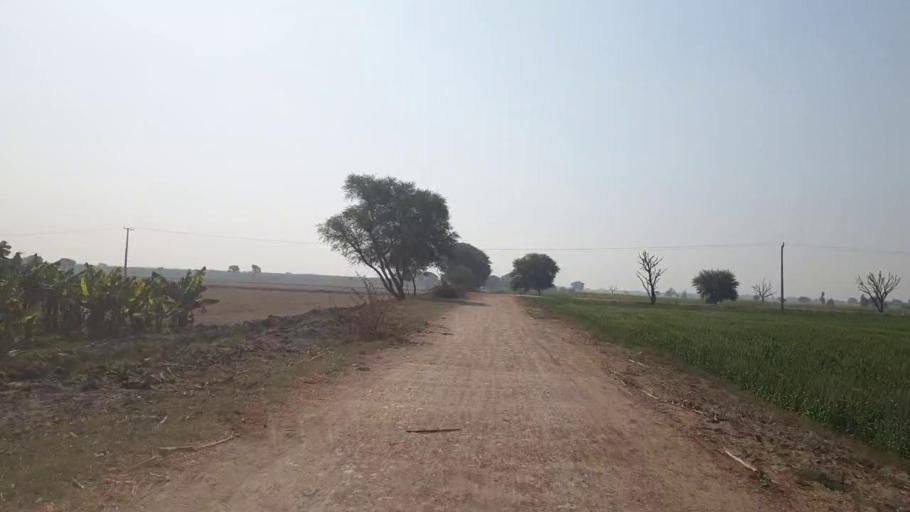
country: PK
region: Sindh
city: Tando Allahyar
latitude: 25.6120
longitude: 68.7362
